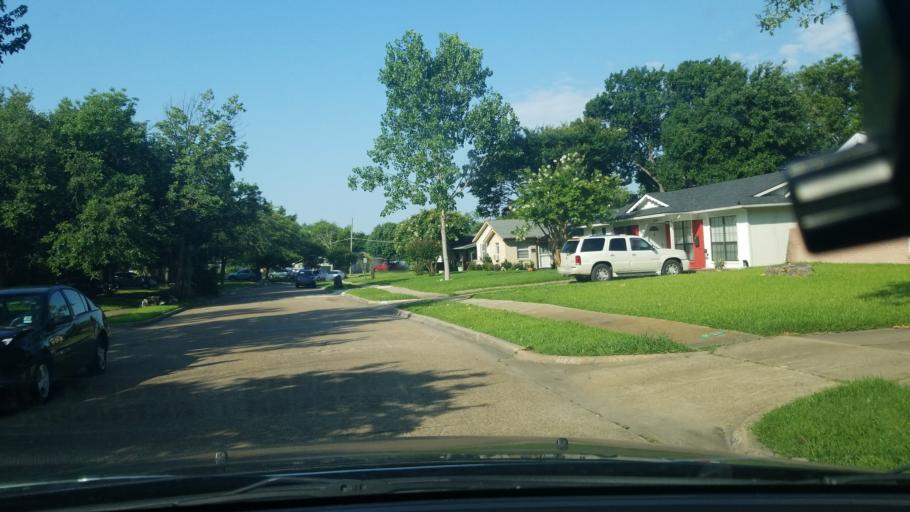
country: US
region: Texas
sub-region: Dallas County
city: Mesquite
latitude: 32.8263
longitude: -96.6362
